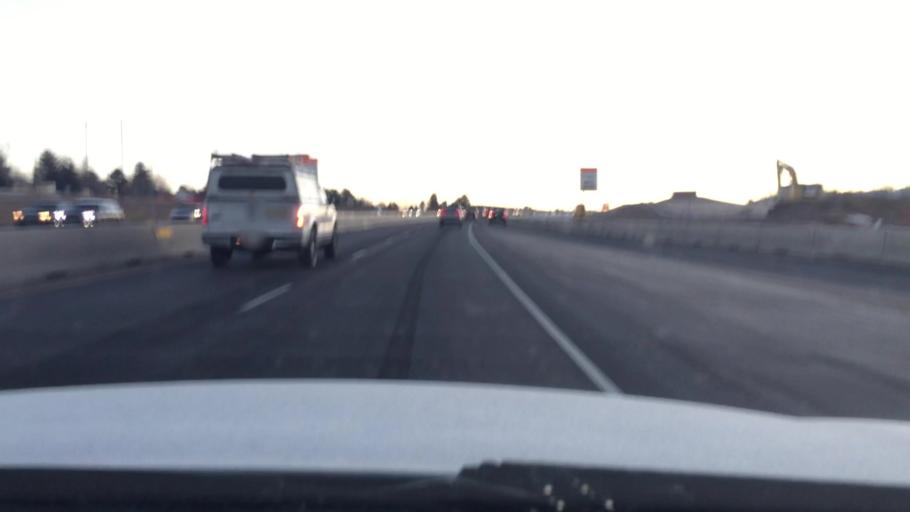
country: US
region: Colorado
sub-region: Douglas County
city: Highlands Ranch
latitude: 39.5651
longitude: -104.9833
